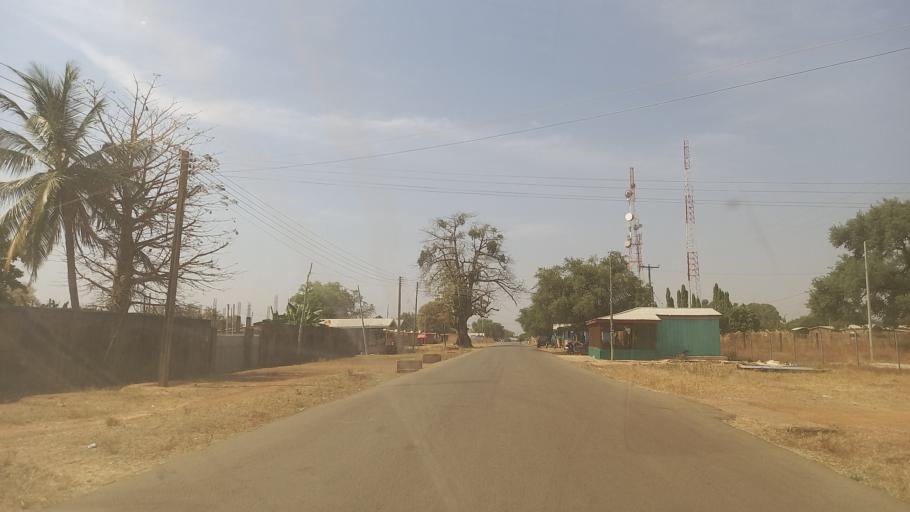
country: GH
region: Upper East
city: Navrongo
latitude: 10.8828
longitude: -1.0811
